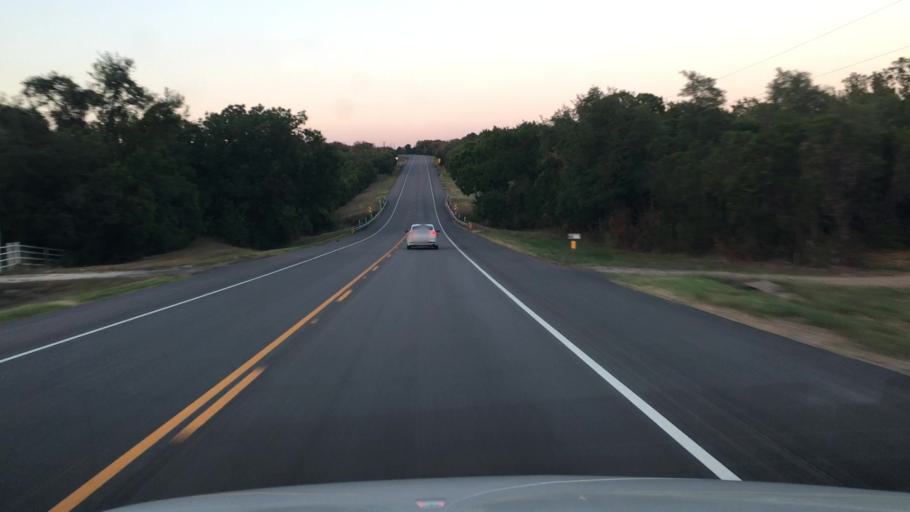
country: US
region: Texas
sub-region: Somervell County
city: Glen Rose
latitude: 32.1929
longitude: -97.8193
